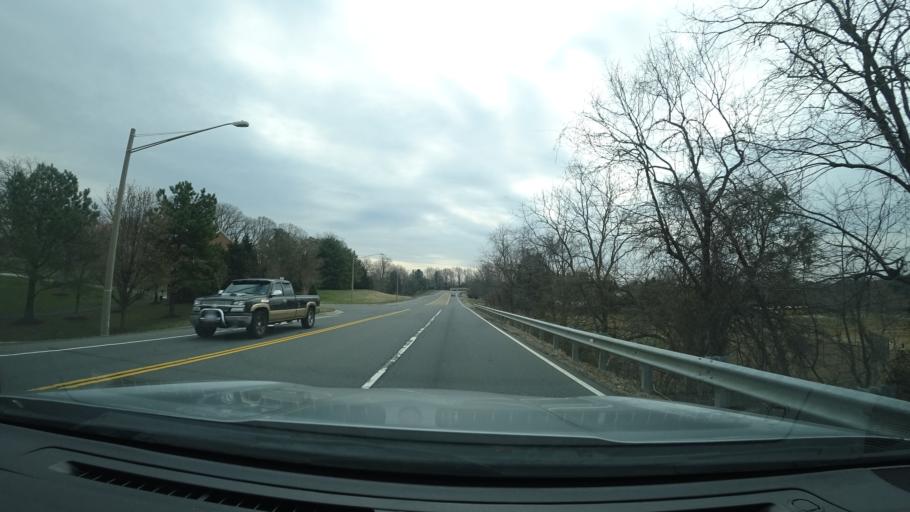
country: US
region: Virginia
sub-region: Fairfax County
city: Reston
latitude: 38.9738
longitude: -77.3147
